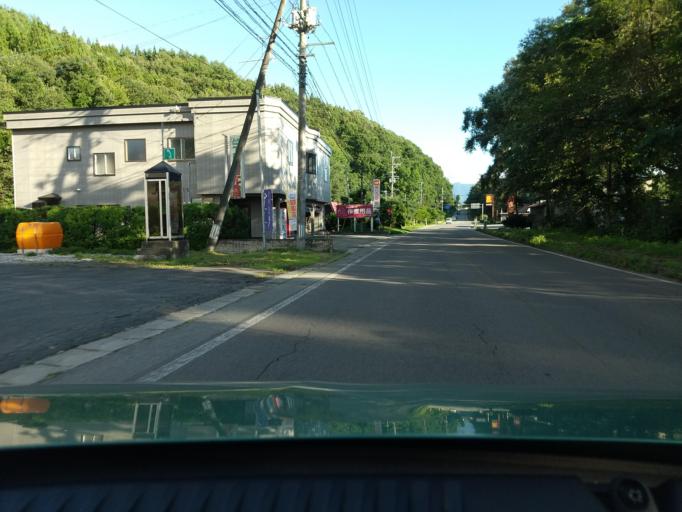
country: JP
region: Akita
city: Kakunodatemachi
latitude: 39.7378
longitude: 140.7175
